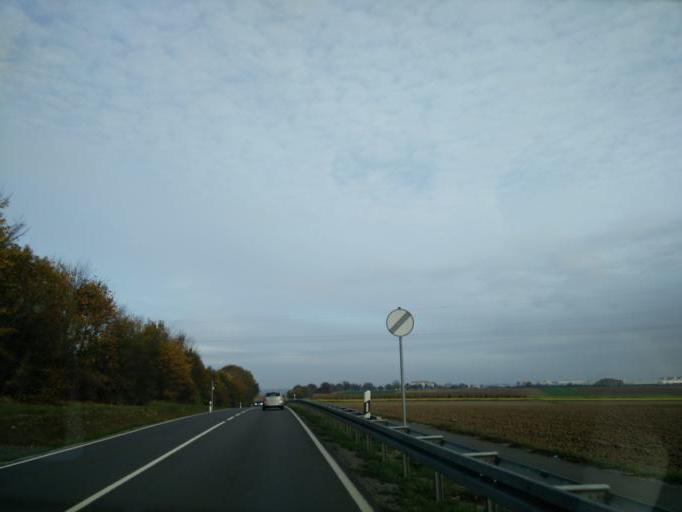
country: DE
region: Baden-Wuerttemberg
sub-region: Regierungsbezirk Stuttgart
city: Holzgerlingen
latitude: 48.6177
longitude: 9.0238
